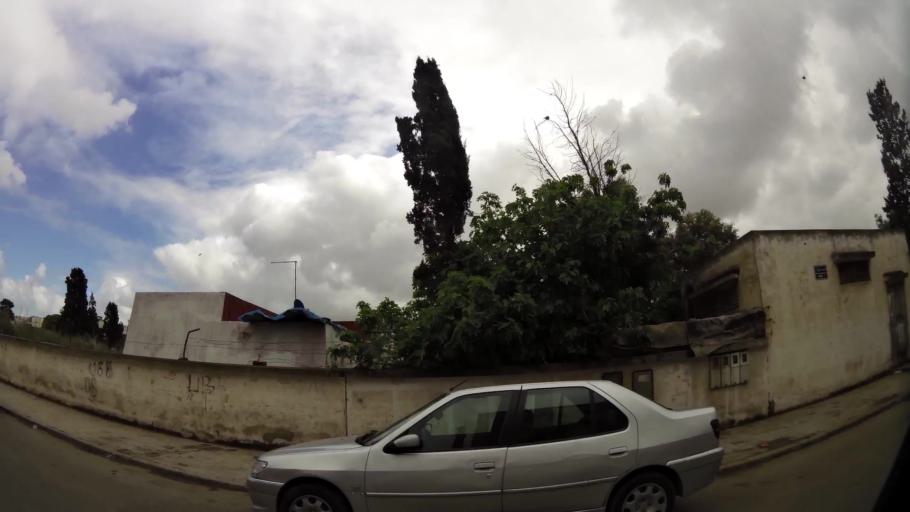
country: MA
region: Grand Casablanca
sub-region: Mediouna
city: Tit Mellil
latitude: 33.6118
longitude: -7.4922
